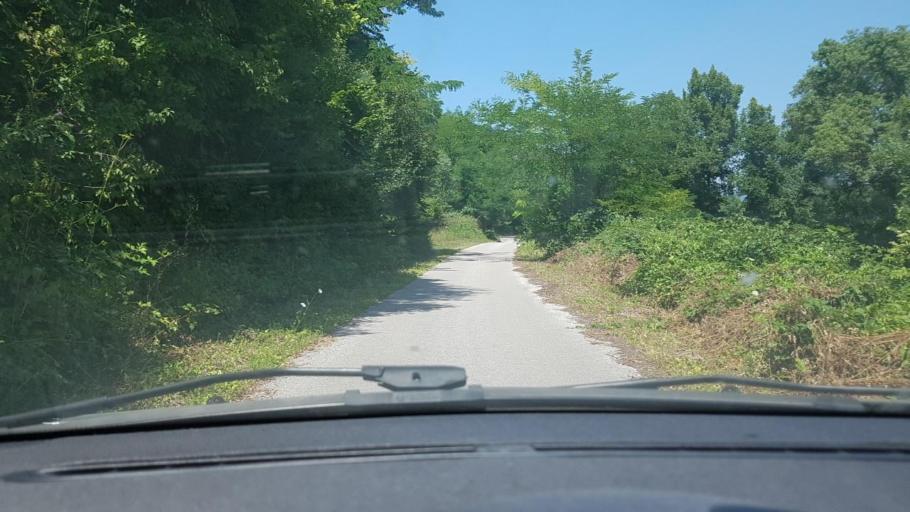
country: BA
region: Federation of Bosnia and Herzegovina
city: Orasac
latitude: 44.5622
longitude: 16.0819
